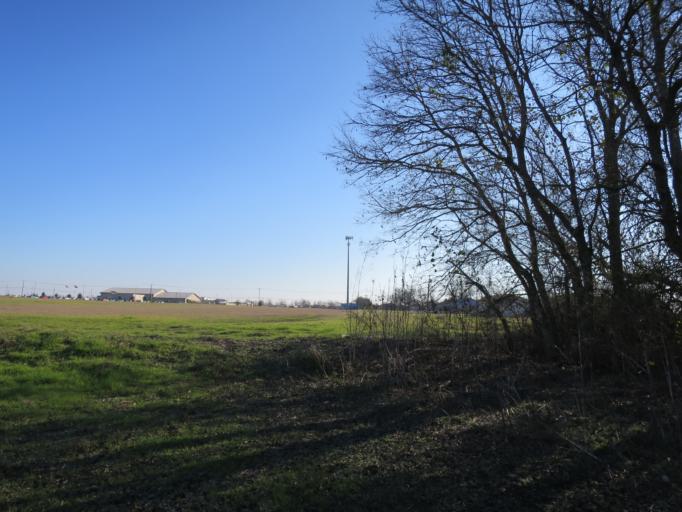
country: US
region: Texas
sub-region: Williamson County
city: Round Rock
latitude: 30.5404
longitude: -97.6173
